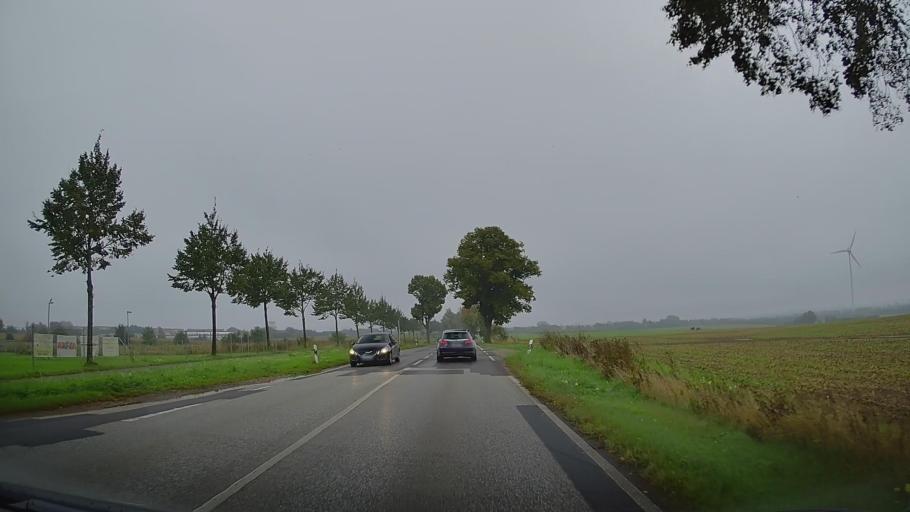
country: DE
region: Mecklenburg-Vorpommern
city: Wismar
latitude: 53.9010
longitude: 11.4051
